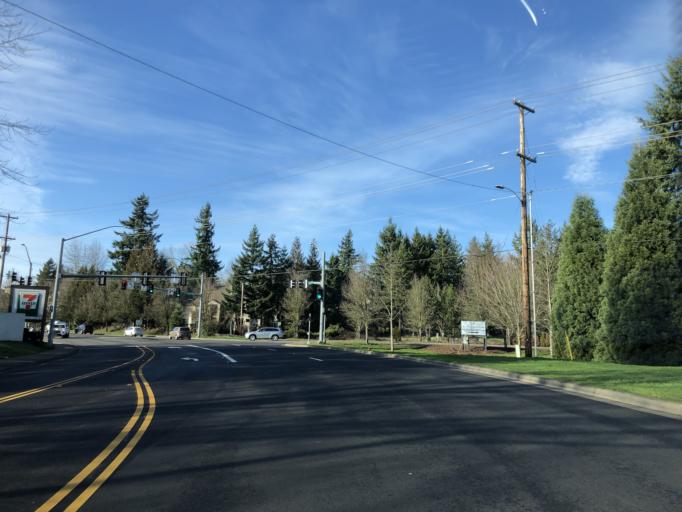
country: US
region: Oregon
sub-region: Washington County
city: Tualatin
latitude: 45.3823
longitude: -122.7443
